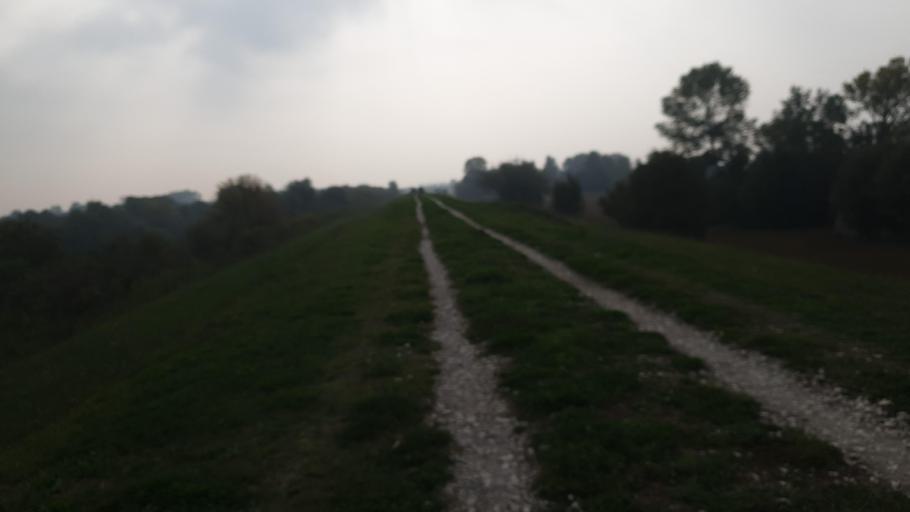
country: IT
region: Veneto
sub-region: Provincia di Venezia
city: Campolongo Maggiore
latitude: 45.3480
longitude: 12.0478
